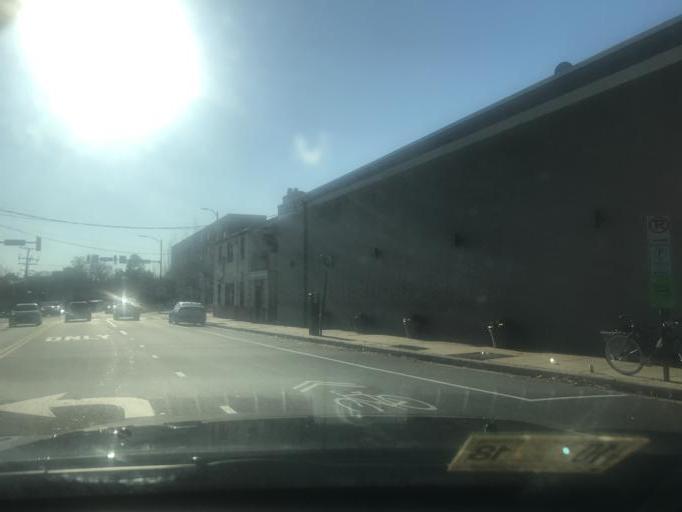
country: US
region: Virginia
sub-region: Arlington County
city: Arlington
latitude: 38.8932
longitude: -77.0802
